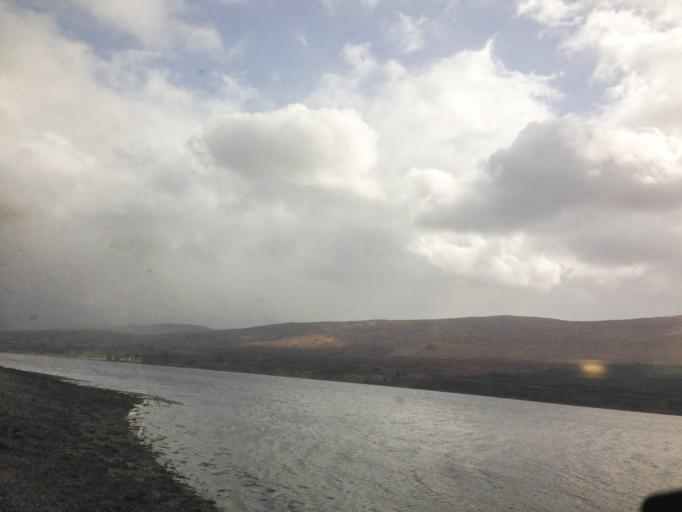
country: GB
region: Scotland
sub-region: Highland
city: Fort William
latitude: 56.8539
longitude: -5.2607
